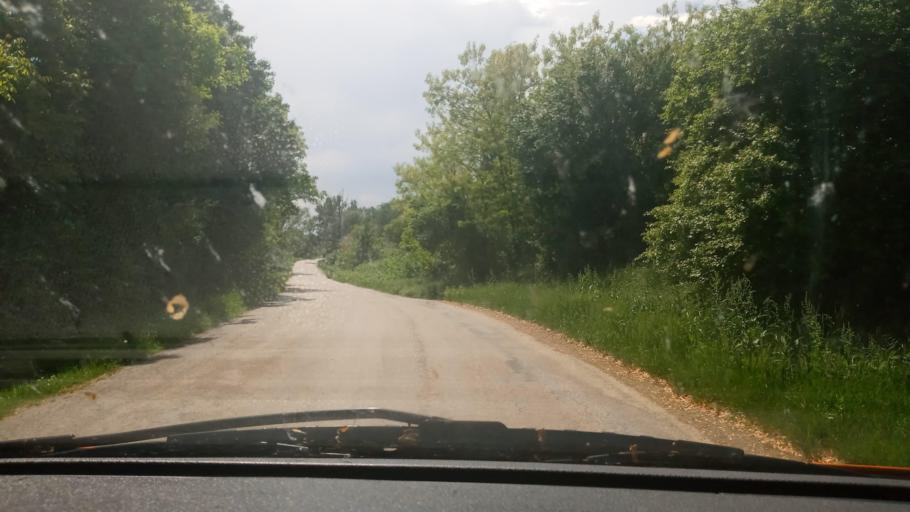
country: HU
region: Baranya
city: Beremend
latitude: 45.8221
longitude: 18.3773
